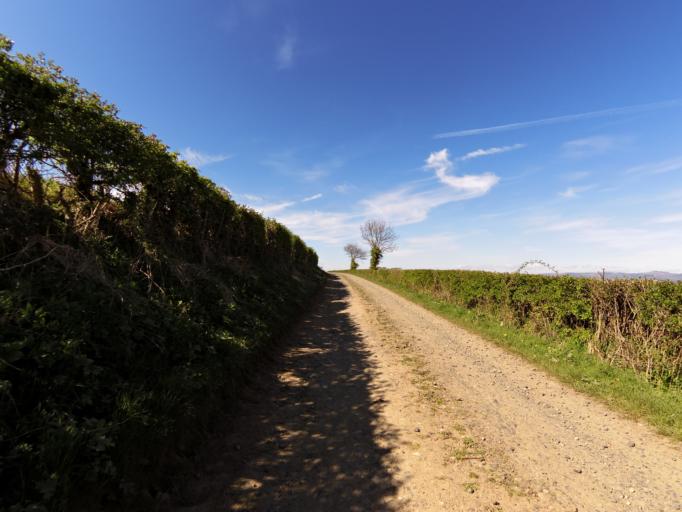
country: GB
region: Scotland
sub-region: Fife
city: Cupar
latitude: 56.4054
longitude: -3.0472
